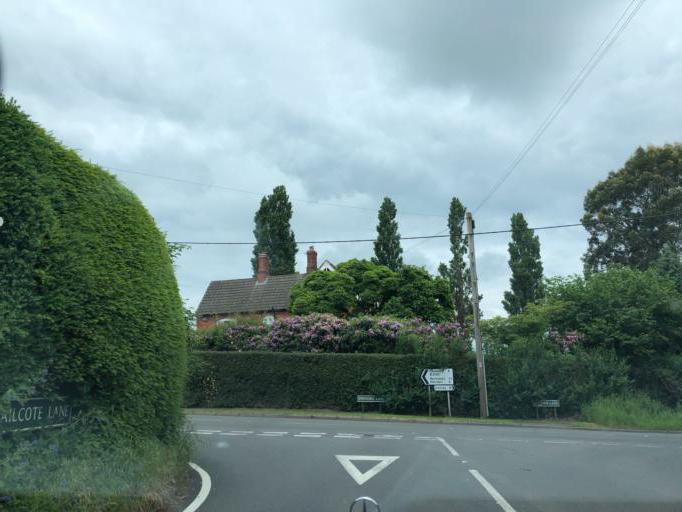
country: GB
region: England
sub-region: Solihull
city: Berkswell
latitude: 52.3951
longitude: -1.6142
